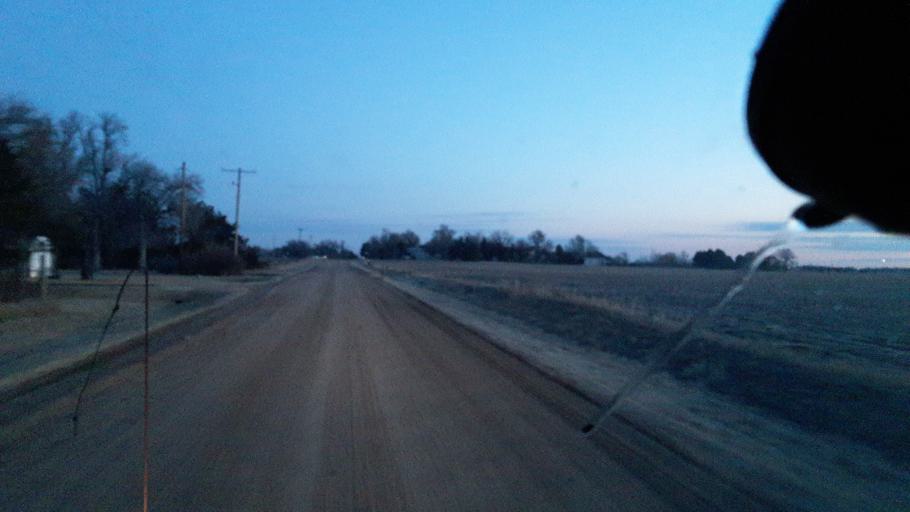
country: US
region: Kansas
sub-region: Reno County
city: South Hutchinson
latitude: 37.9968
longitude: -97.9770
